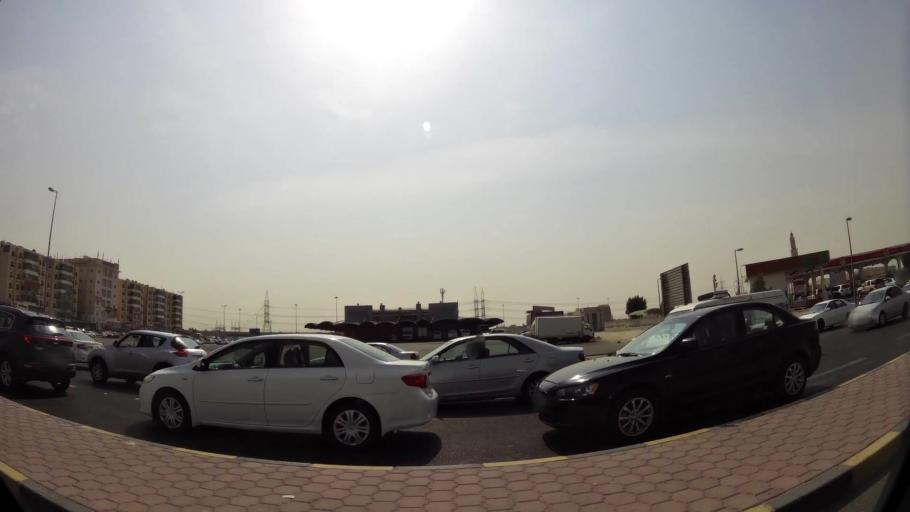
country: KW
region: Al Asimah
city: Ar Rabiyah
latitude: 29.3024
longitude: 47.9047
